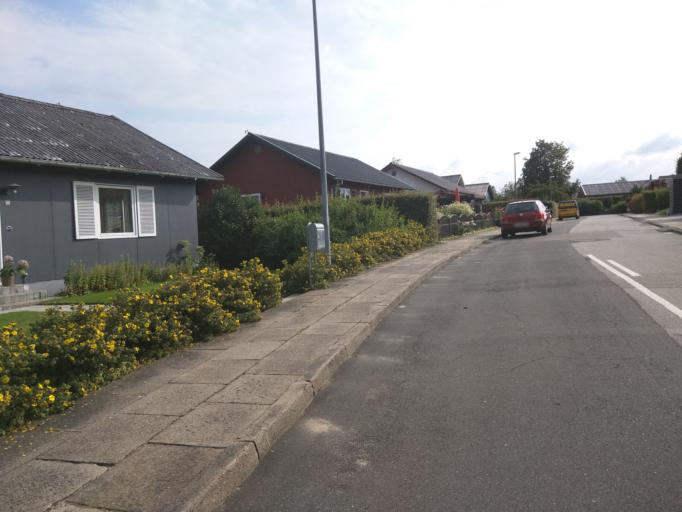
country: DK
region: Central Jutland
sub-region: Viborg Kommune
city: Viborg
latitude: 56.4452
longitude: 9.3829
